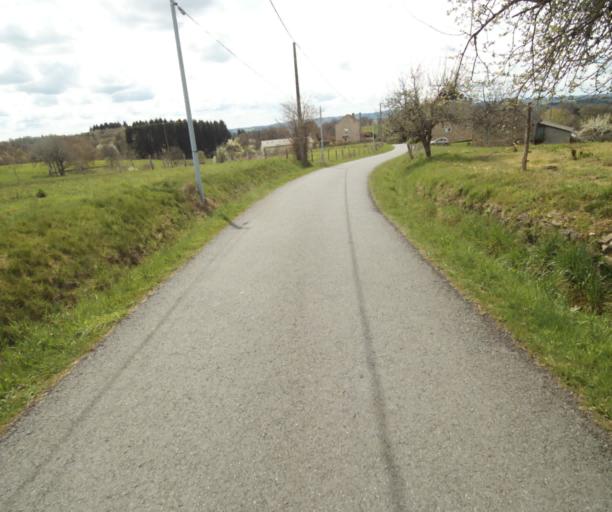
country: FR
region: Limousin
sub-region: Departement de la Correze
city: Laguenne
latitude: 45.1999
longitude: 1.8876
